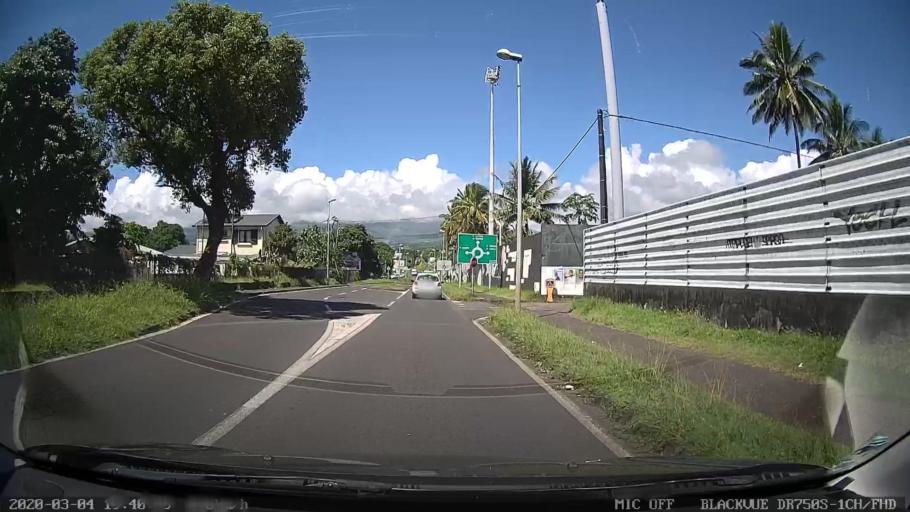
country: RE
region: Reunion
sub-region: Reunion
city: Saint-Benoit
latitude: -21.0457
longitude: 55.7185
